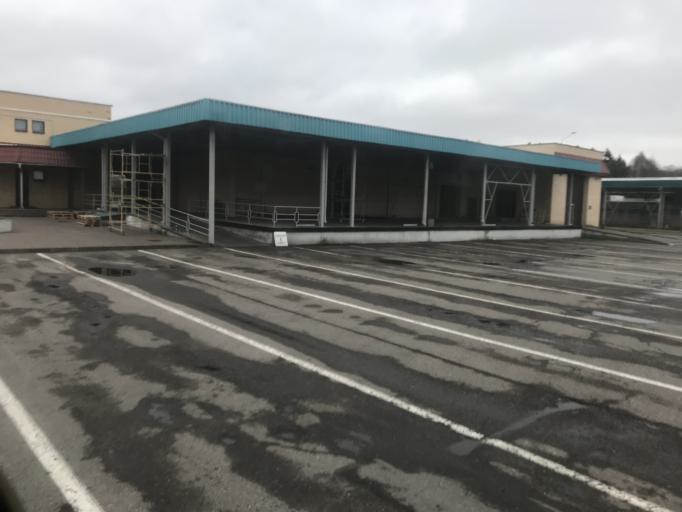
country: BY
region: Grodnenskaya
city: Vyalikaya Byerastavitsa
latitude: 53.1216
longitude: 23.8976
